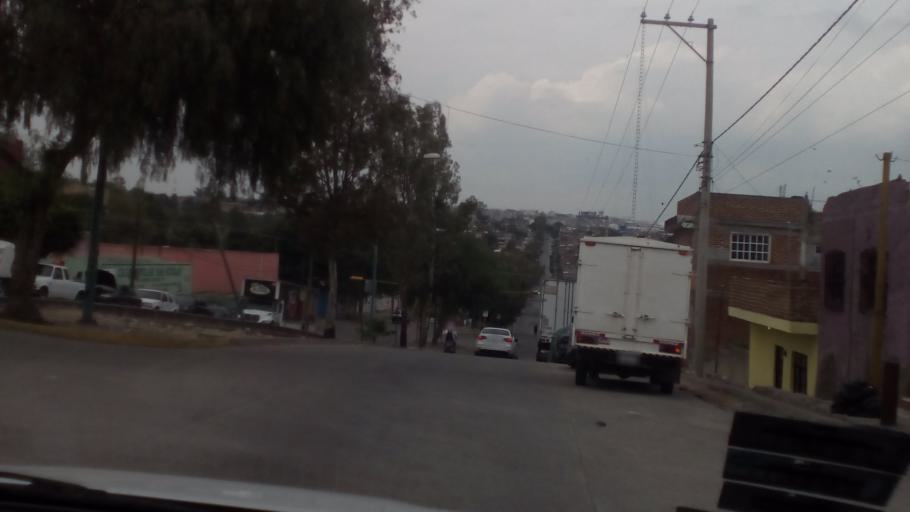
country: MX
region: Guanajuato
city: Leon
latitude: 21.1256
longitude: -101.6957
